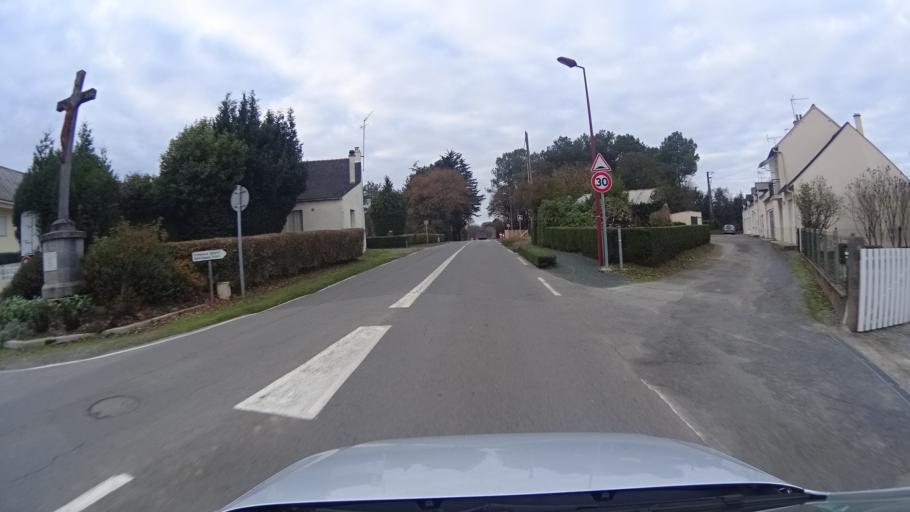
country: FR
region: Pays de la Loire
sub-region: Departement de la Loire-Atlantique
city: Avessac
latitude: 47.6506
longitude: -1.9926
